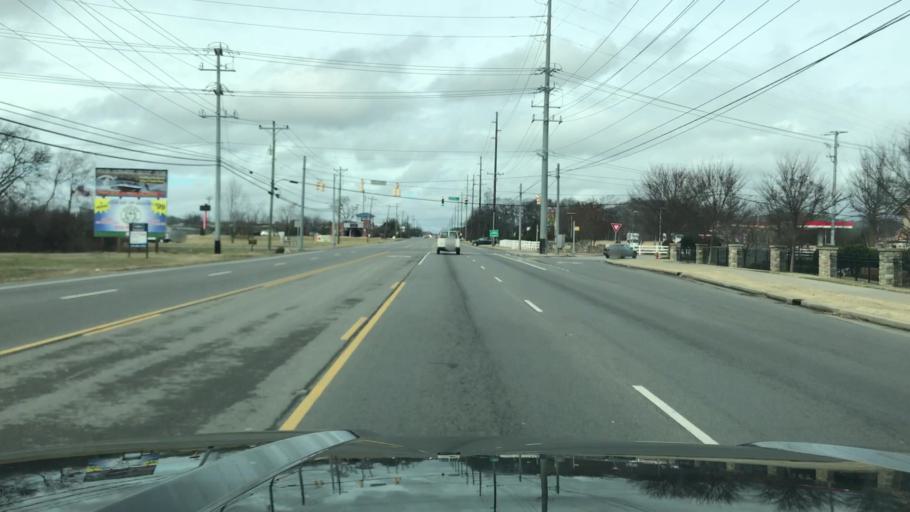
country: US
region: Tennessee
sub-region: Rutherford County
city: La Vergne
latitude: 36.0278
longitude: -86.5898
